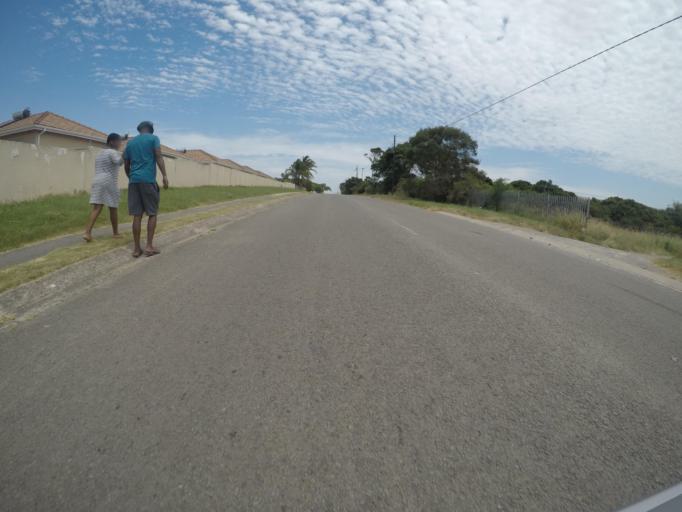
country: ZA
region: Eastern Cape
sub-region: Buffalo City Metropolitan Municipality
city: East London
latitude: -32.9823
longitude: 27.8607
